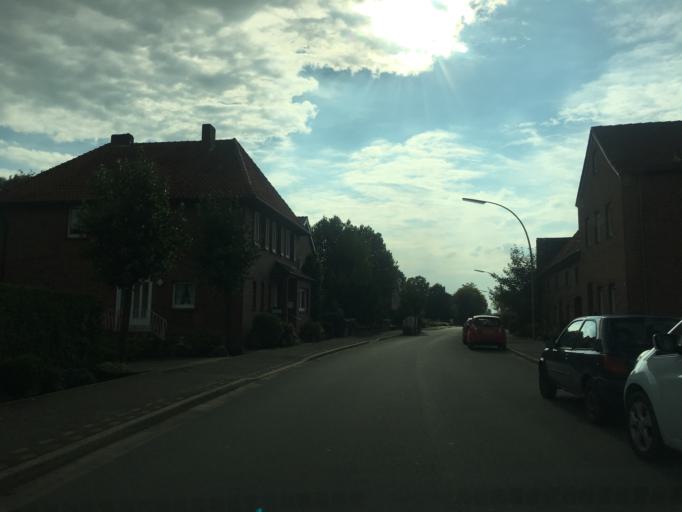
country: DE
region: North Rhine-Westphalia
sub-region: Regierungsbezirk Munster
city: Nordkirchen
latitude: 51.7091
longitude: 7.5456
